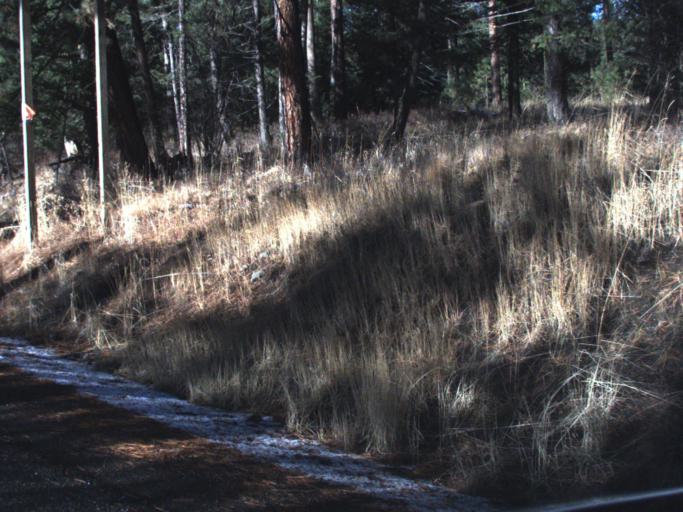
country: US
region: Washington
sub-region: Asotin County
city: Asotin
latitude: 46.0898
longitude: -117.1623
